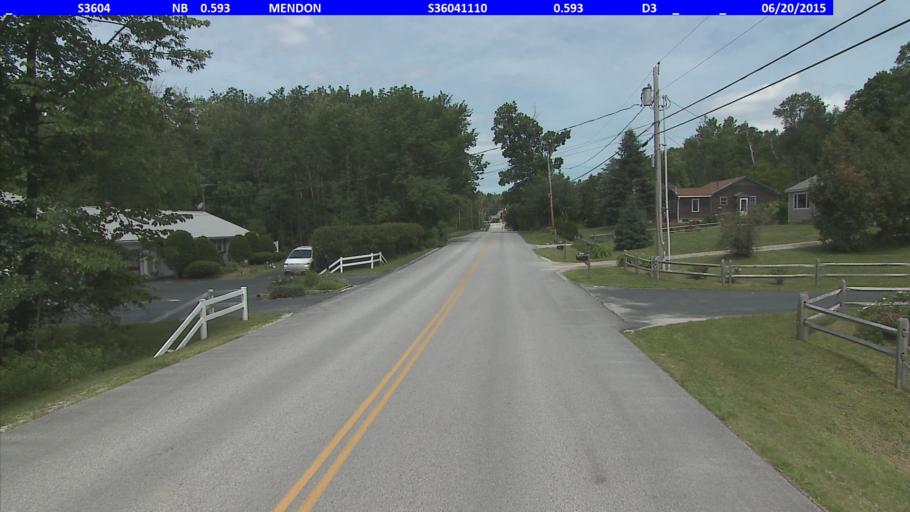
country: US
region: Vermont
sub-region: Rutland County
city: Rutland
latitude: 43.6307
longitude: -72.9372
